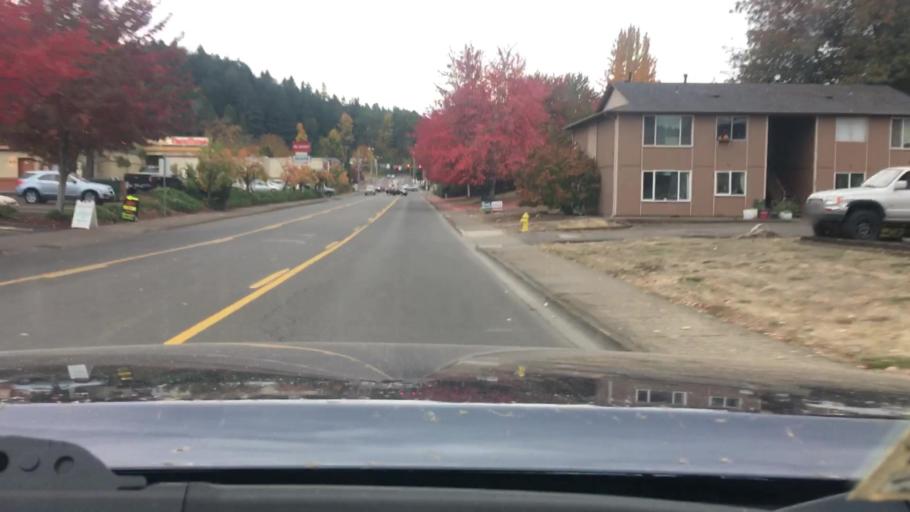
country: US
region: Oregon
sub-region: Lane County
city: Cottage Grove
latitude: 43.7992
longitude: -123.0488
